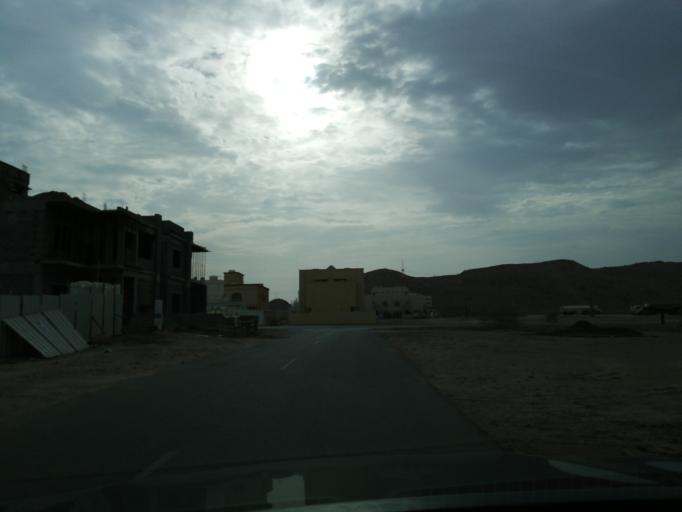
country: OM
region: Muhafazat Masqat
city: Bawshar
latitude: 23.4773
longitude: 58.3082
